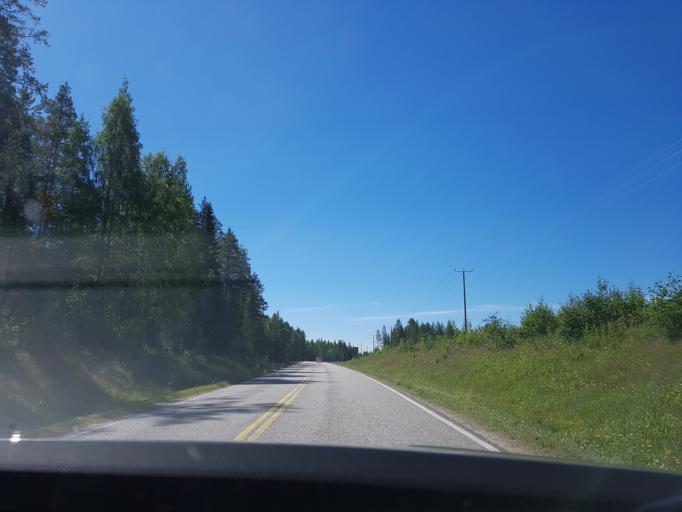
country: FI
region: Kainuu
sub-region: Kehys-Kainuu
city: Kuhmo
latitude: 64.1739
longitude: 29.6598
